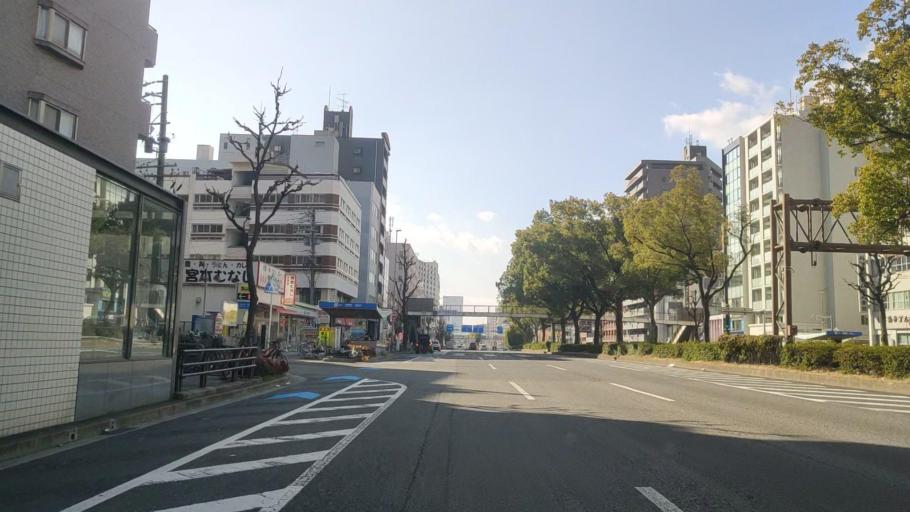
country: JP
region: Aichi
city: Nagoya-shi
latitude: 35.1606
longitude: 136.8984
